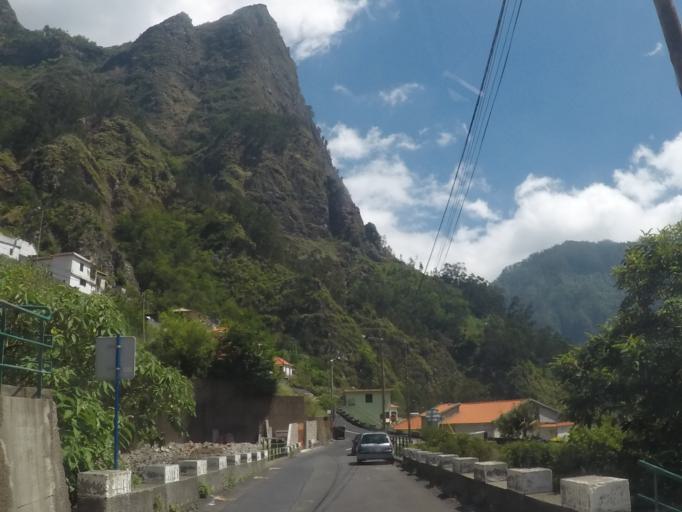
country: PT
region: Madeira
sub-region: Camara de Lobos
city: Curral das Freiras
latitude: 32.7167
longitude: -16.9684
